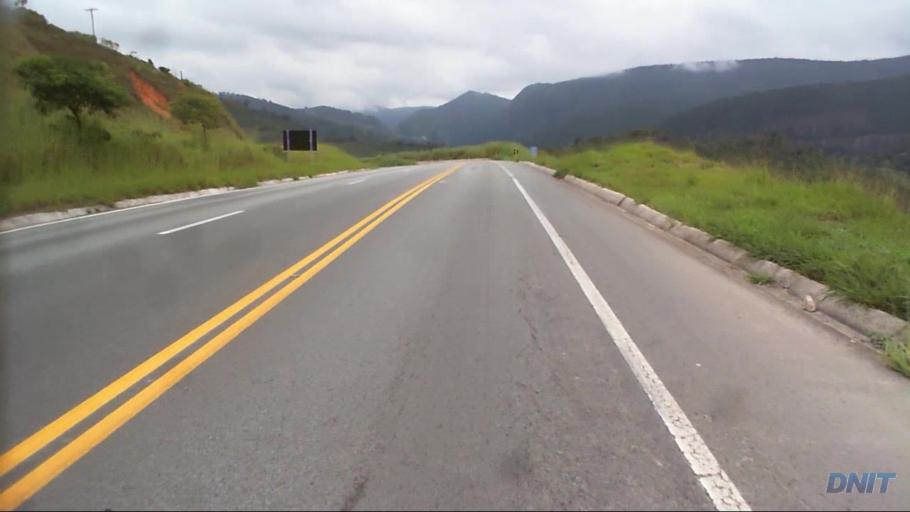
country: BR
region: Minas Gerais
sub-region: Nova Era
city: Nova Era
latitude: -19.6413
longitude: -42.9024
